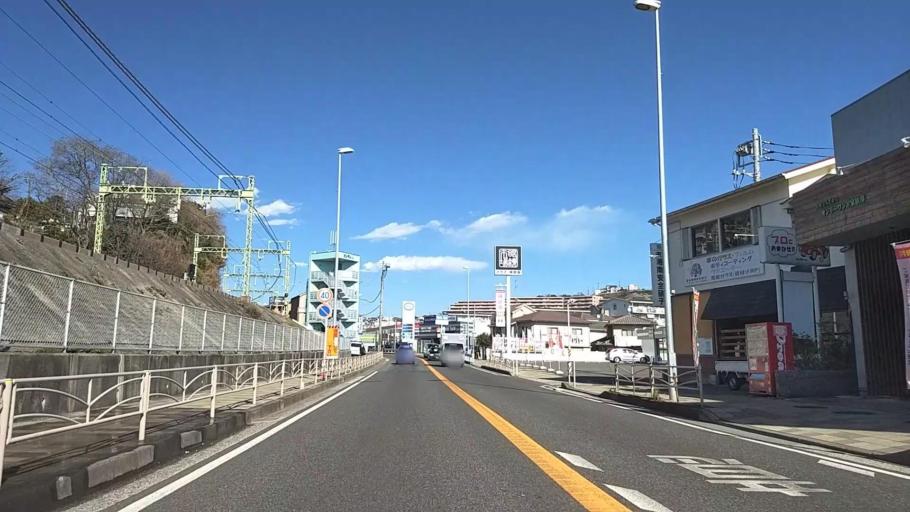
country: JP
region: Kanagawa
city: Zushi
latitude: 35.3506
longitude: 139.6263
